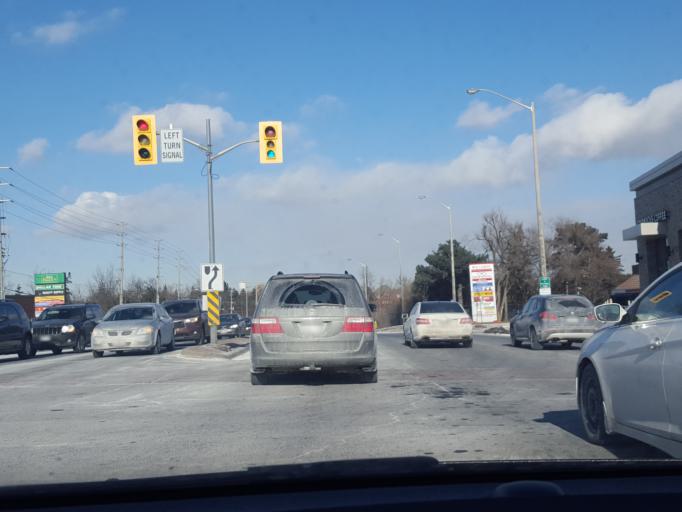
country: CA
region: Ontario
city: Brampton
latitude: 43.6660
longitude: -79.7331
